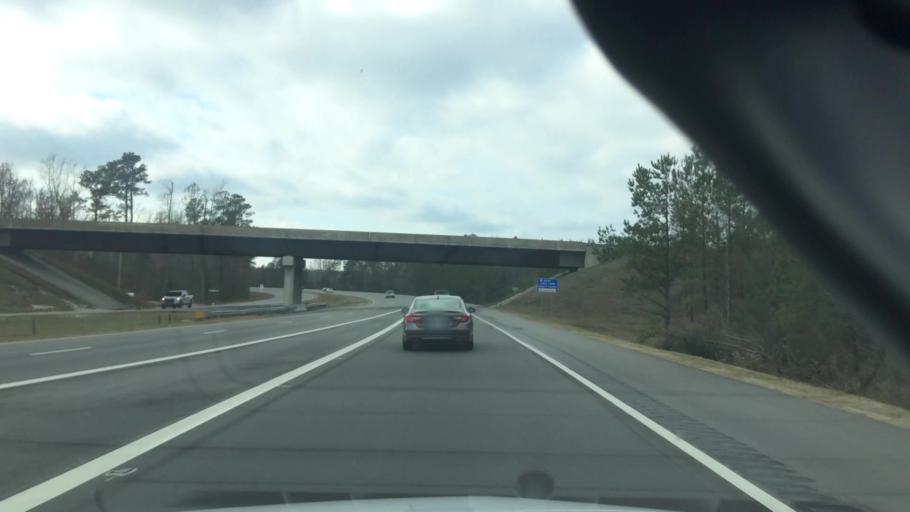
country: US
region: North Carolina
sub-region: New Hanover County
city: Skippers Corner
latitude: 34.3184
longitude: -77.8808
